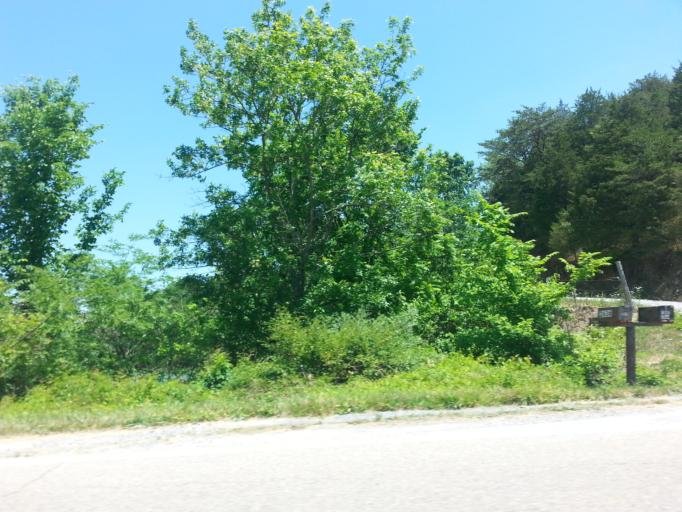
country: US
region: Tennessee
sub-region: Jefferson County
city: Dandridge
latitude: 35.9538
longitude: -83.3662
